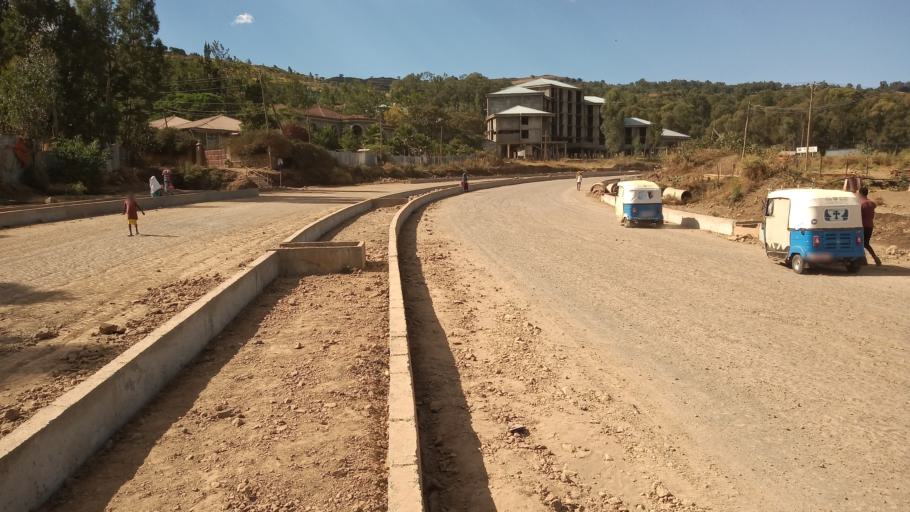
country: ET
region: Amhara
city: Gondar
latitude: 12.5707
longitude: 37.4329
